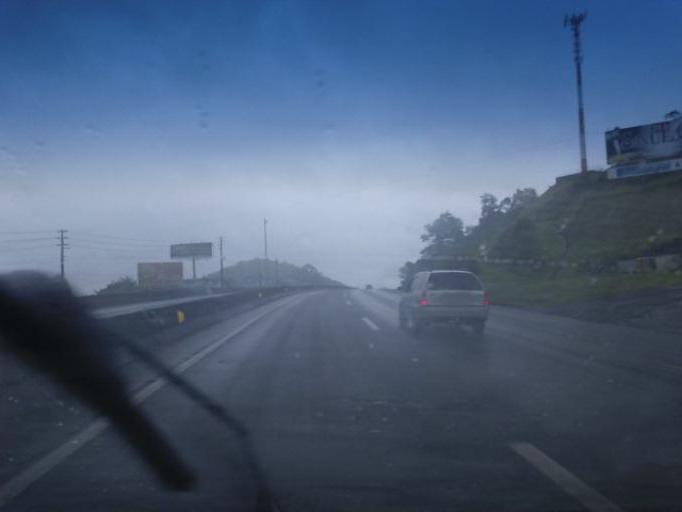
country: BR
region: Santa Catarina
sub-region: Barra Velha
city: Barra Velha
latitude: -26.7105
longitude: -48.7028
